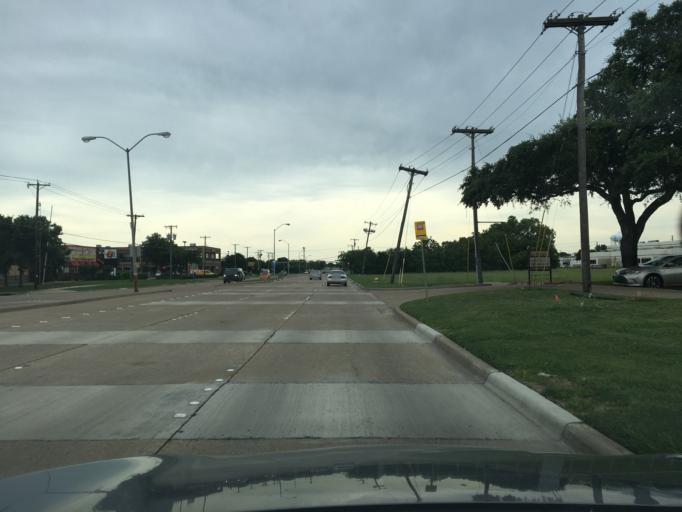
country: US
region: Texas
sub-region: Dallas County
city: Richardson
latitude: 32.9635
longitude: -96.7000
